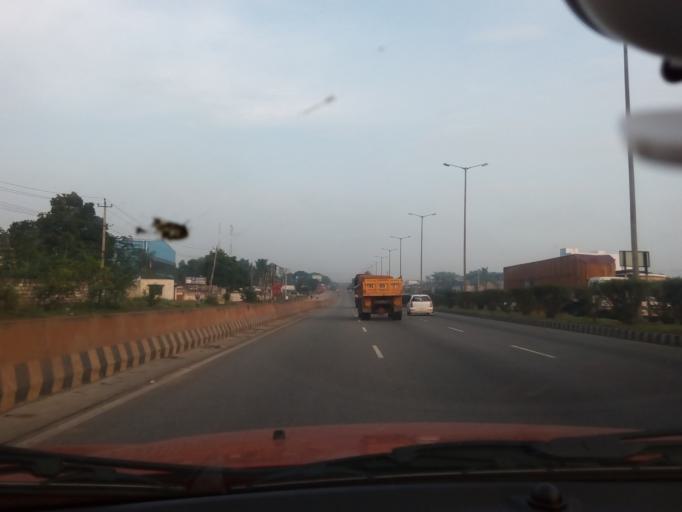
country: IN
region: Karnataka
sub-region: Bangalore Rural
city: Nelamangala
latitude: 13.0858
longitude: 77.4111
